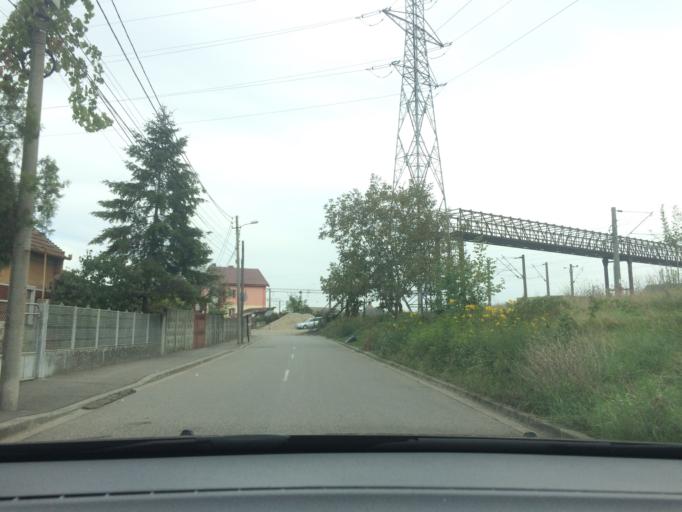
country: RO
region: Timis
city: Timisoara
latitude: 45.7492
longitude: 21.1888
